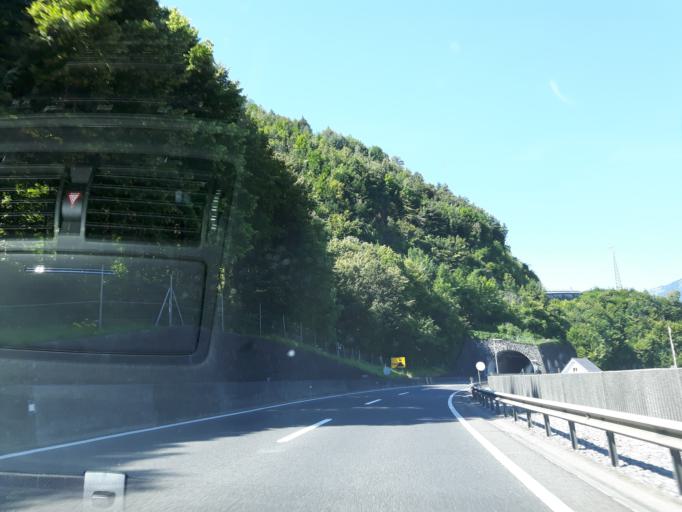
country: CH
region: Saint Gallen
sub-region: Wahlkreis See-Gaster
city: Amden
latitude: 47.1144
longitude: 9.1857
